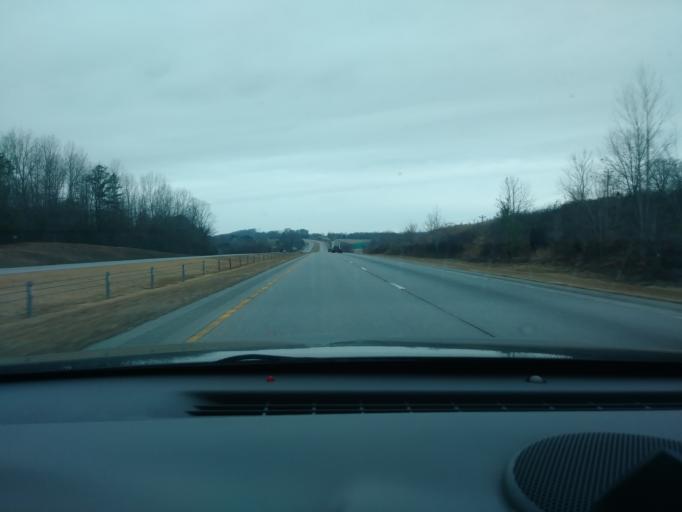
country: US
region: North Carolina
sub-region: Yadkin County
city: Jonesville
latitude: 36.1359
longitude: -80.8572
